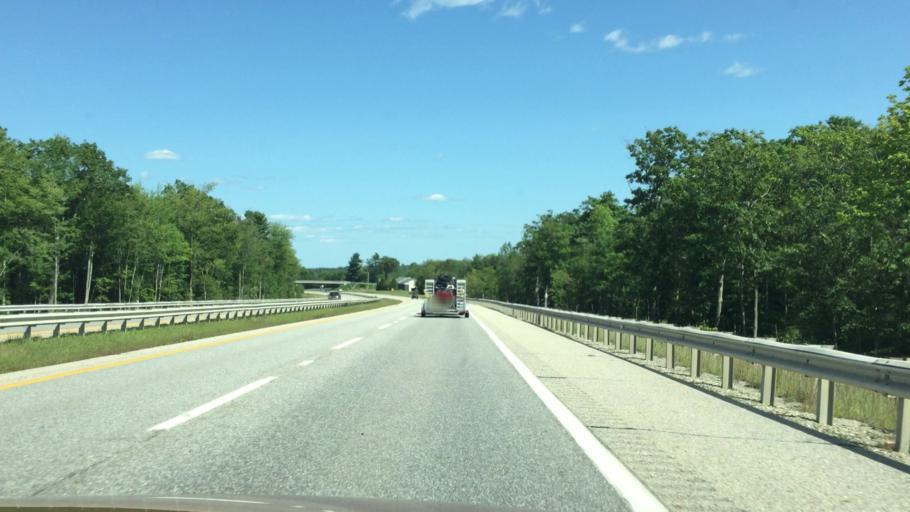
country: US
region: Maine
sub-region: Kennebec County
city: Monmouth
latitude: 44.1252
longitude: -69.9754
